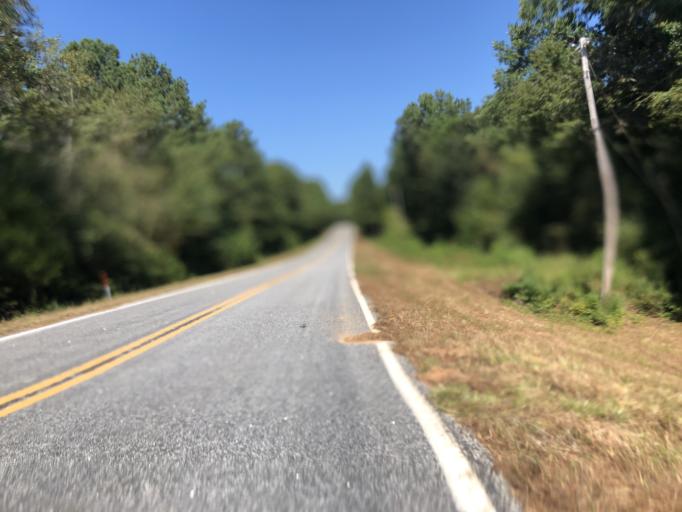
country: US
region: Georgia
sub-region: Heard County
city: Franklin
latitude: 33.3808
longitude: -84.9873
